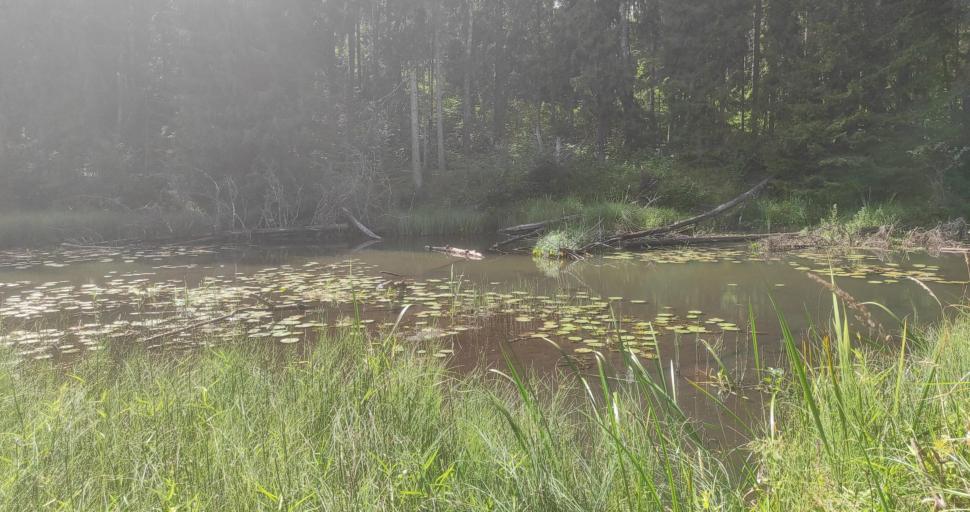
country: LV
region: Kuldigas Rajons
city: Kuldiga
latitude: 56.9839
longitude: 21.7751
